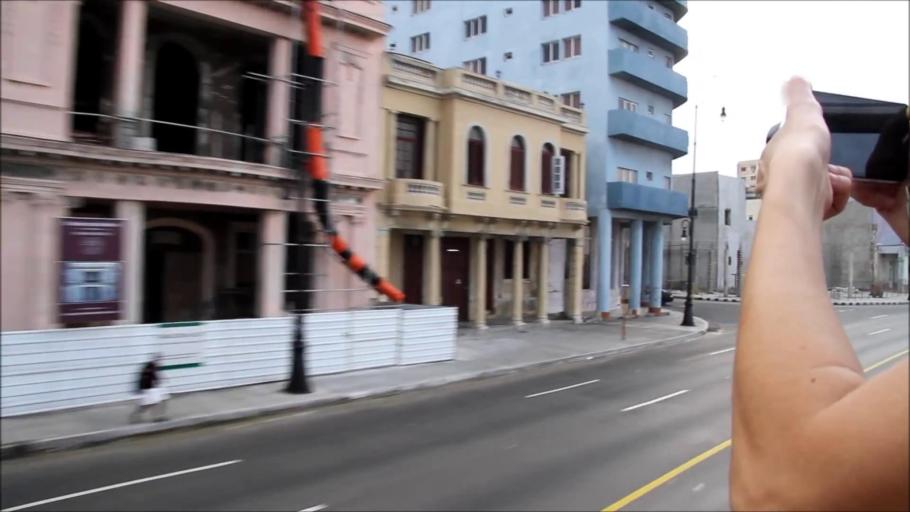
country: CU
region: La Habana
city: Centro Habana
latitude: 23.1424
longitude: -82.3638
